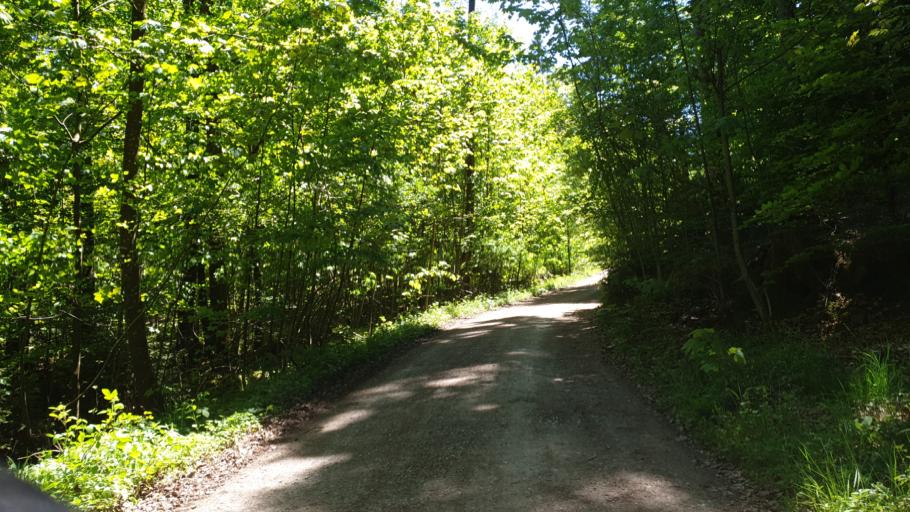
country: DE
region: Bavaria
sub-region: Upper Bavaria
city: Obersochering
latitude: 47.7728
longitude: 11.2494
